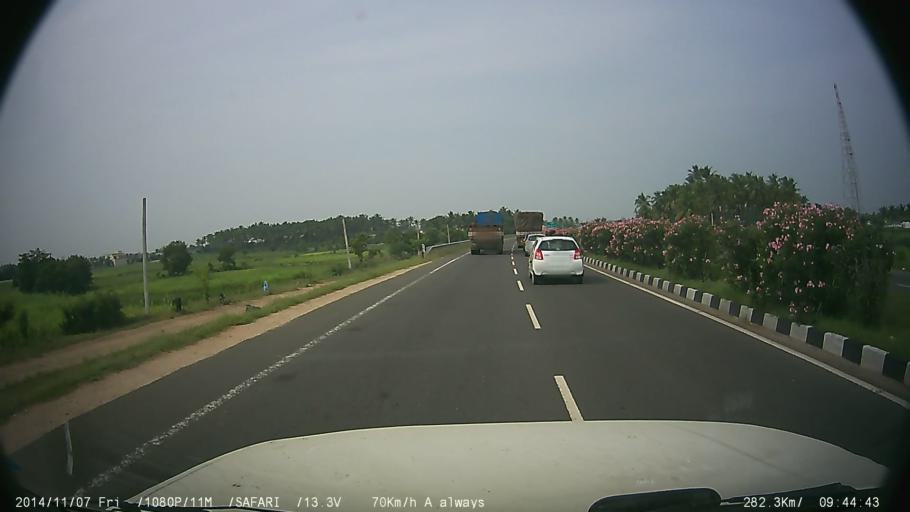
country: IN
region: Tamil Nadu
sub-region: Erode
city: Perundurai
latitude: 11.2927
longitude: 77.5893
